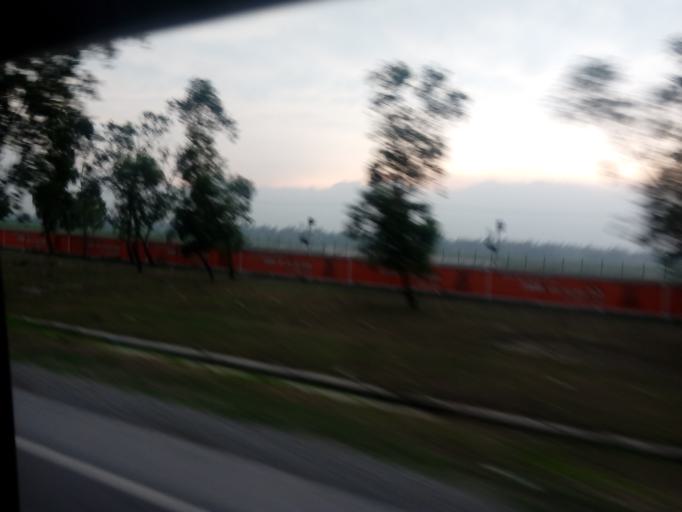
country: BD
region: Rajshahi
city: Sirajganj
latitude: 24.3947
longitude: 89.7309
